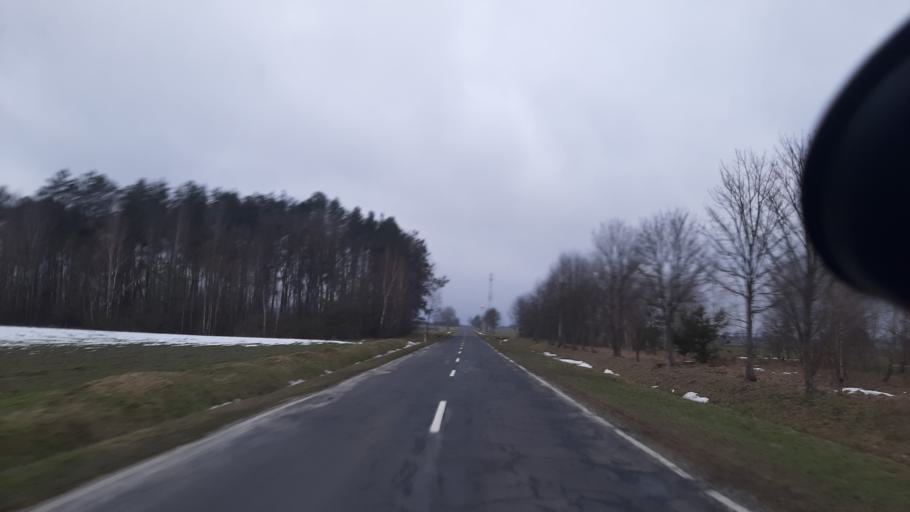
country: PL
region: Lublin Voivodeship
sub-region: Powiat wlodawski
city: Hansk
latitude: 51.5599
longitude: 23.3263
